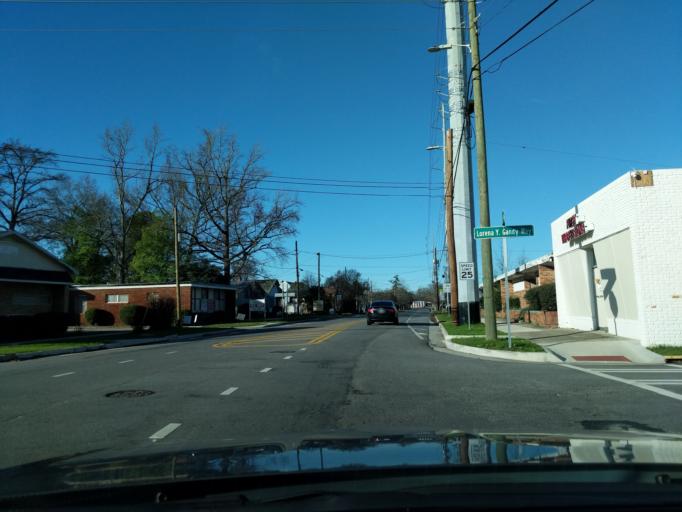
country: US
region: Georgia
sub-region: Richmond County
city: Augusta
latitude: 33.4718
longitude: -81.9963
